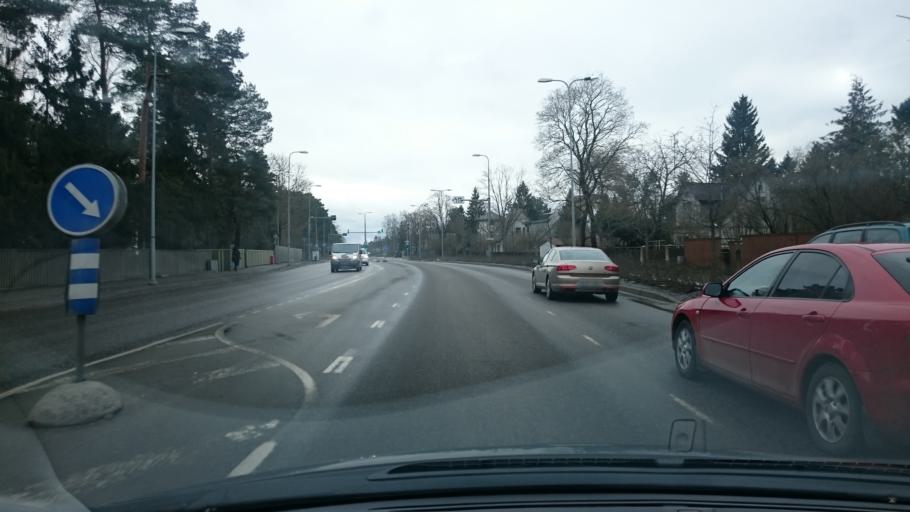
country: EE
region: Harju
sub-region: Tallinna linn
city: Tallinn
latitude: 59.3862
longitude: 24.7176
